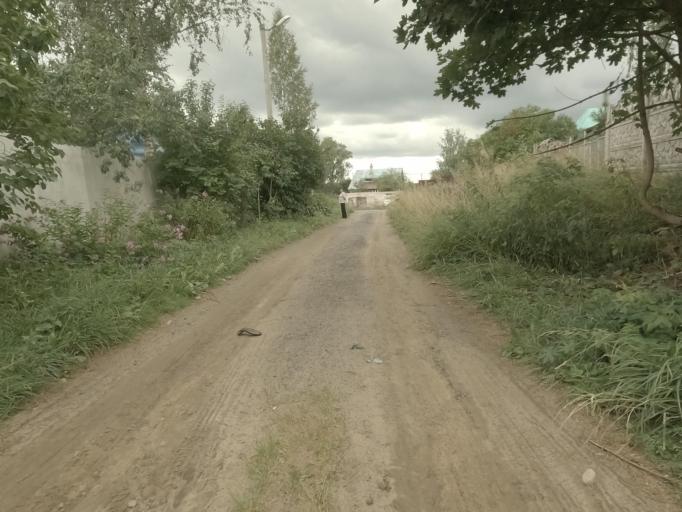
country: RU
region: Leningrad
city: Koltushi
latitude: 59.8875
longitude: 30.6948
